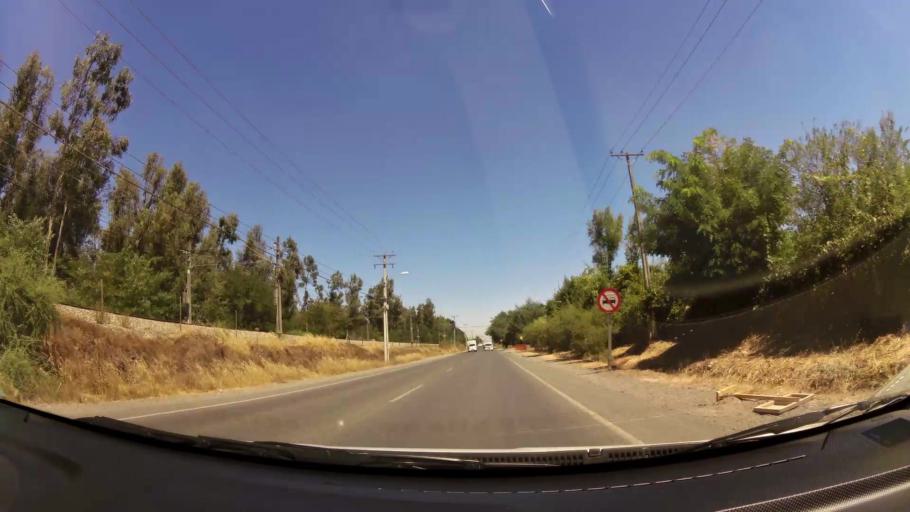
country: CL
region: O'Higgins
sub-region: Provincia de Cachapoal
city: Rancagua
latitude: -34.2341
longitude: -70.7884
